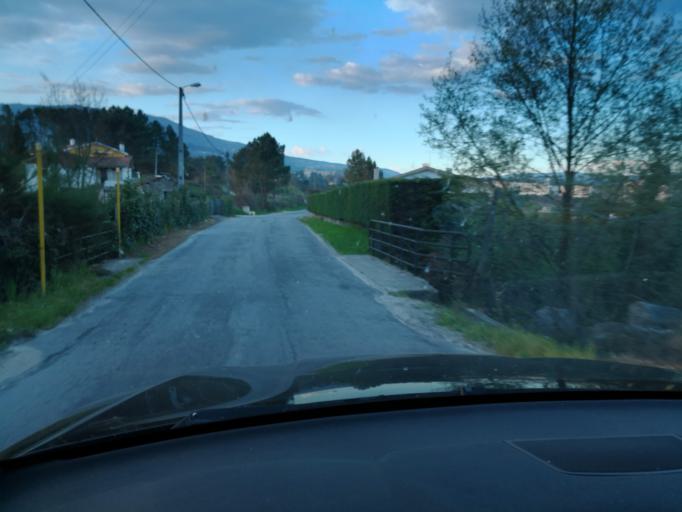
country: PT
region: Vila Real
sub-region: Vila Real
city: Vila Real
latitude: 41.3001
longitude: -7.7638
